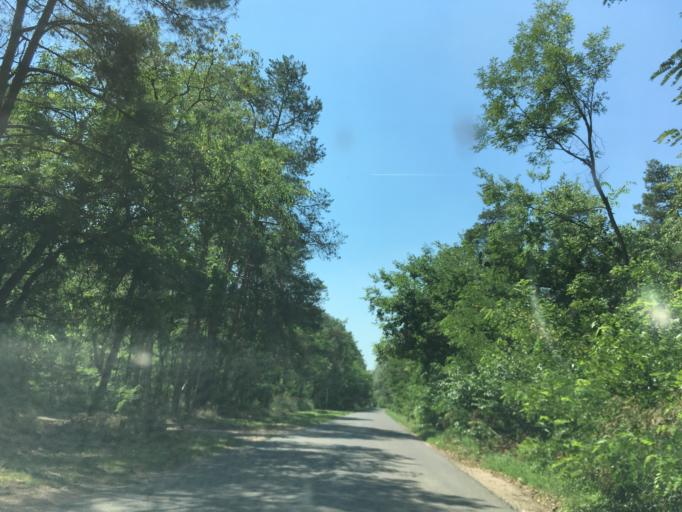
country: HU
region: Hajdu-Bihar
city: Mikepercs
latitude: 47.4756
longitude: 21.7059
